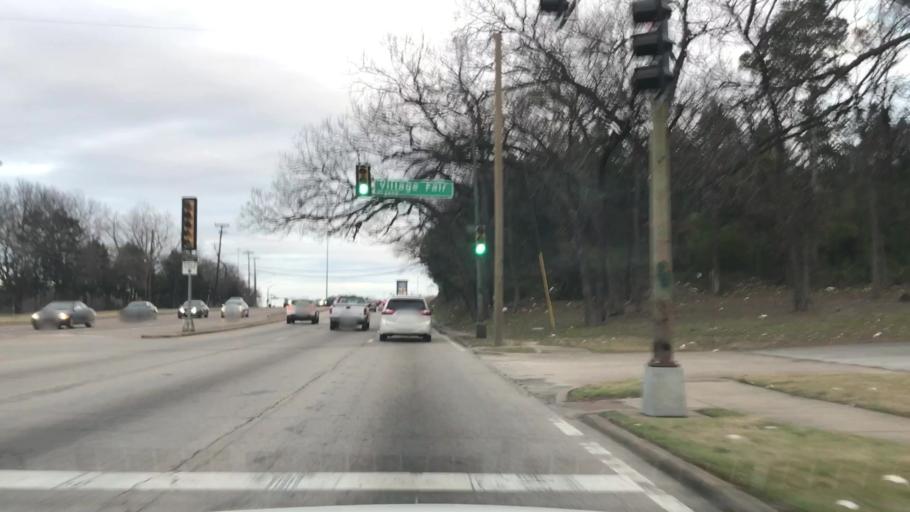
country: US
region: Texas
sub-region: Dallas County
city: Cockrell Hill
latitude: 32.6888
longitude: -96.8288
